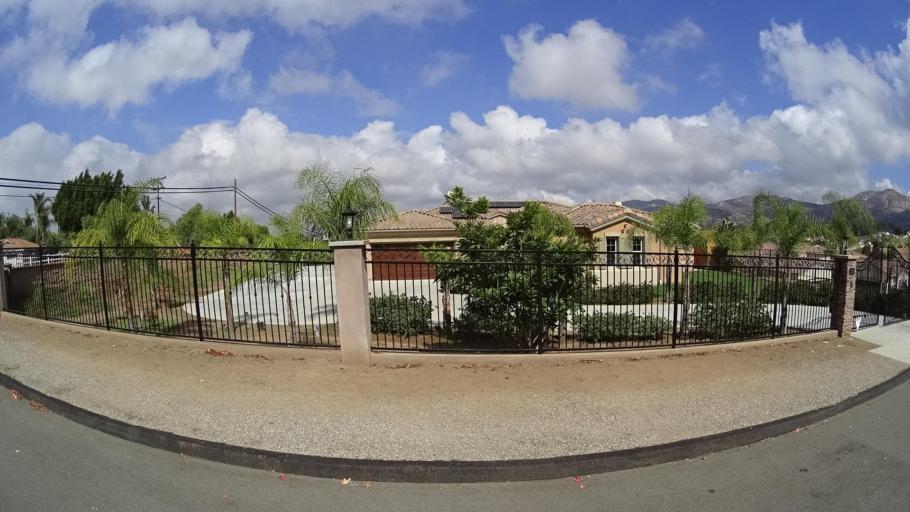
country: US
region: California
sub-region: San Diego County
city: Granite Hills
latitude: 32.7803
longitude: -116.9059
